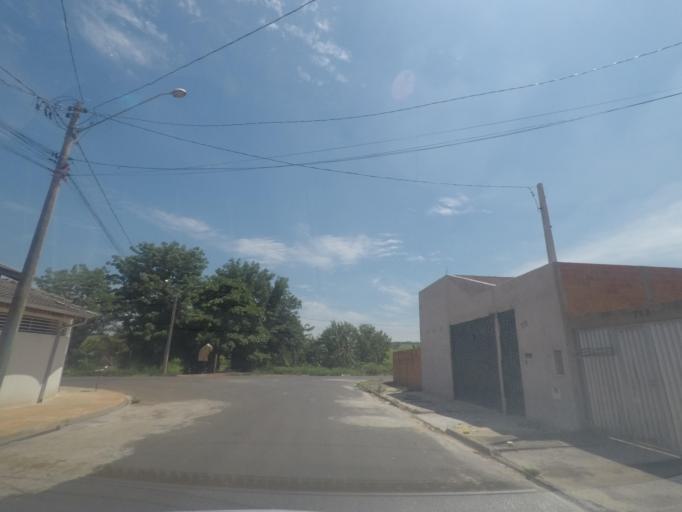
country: BR
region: Sao Paulo
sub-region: Sumare
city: Sumare
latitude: -22.7972
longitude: -47.2667
